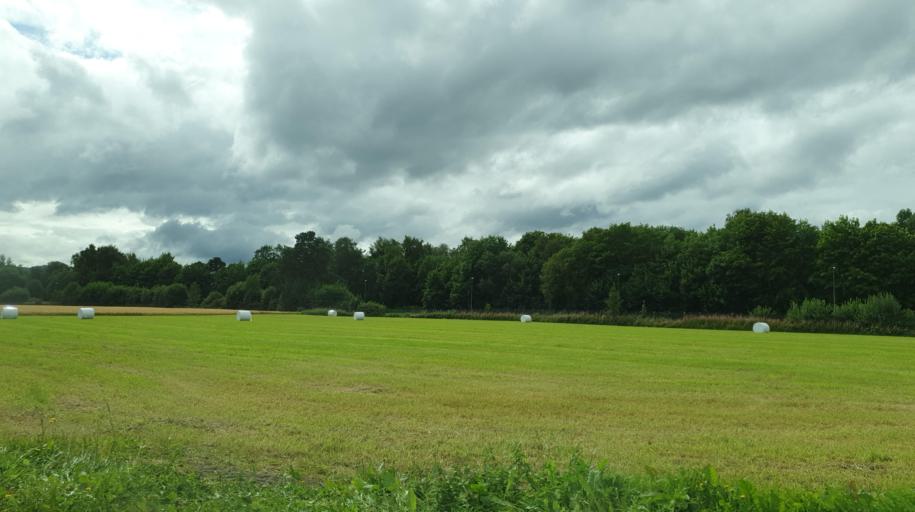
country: NO
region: Nord-Trondelag
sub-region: Stjordal
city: Stjordalshalsen
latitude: 63.4624
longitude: 10.9450
